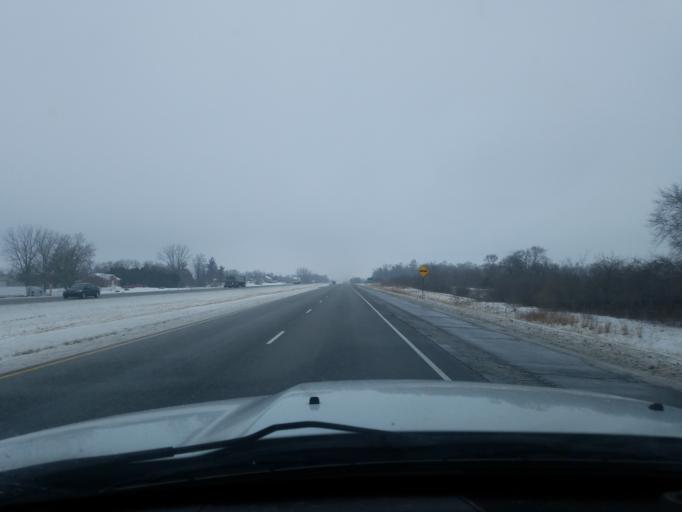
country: US
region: Indiana
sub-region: Fulton County
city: Rochester
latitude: 40.9569
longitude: -86.1682
